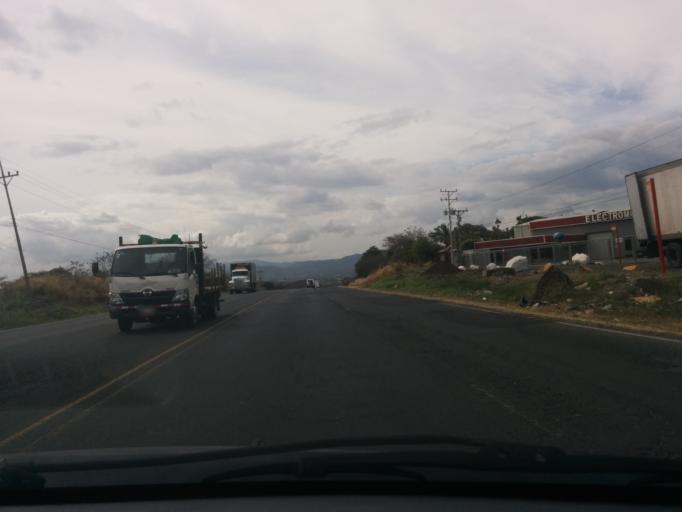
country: CR
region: Alajuela
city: Carrillos
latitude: 9.9979
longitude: -84.2747
